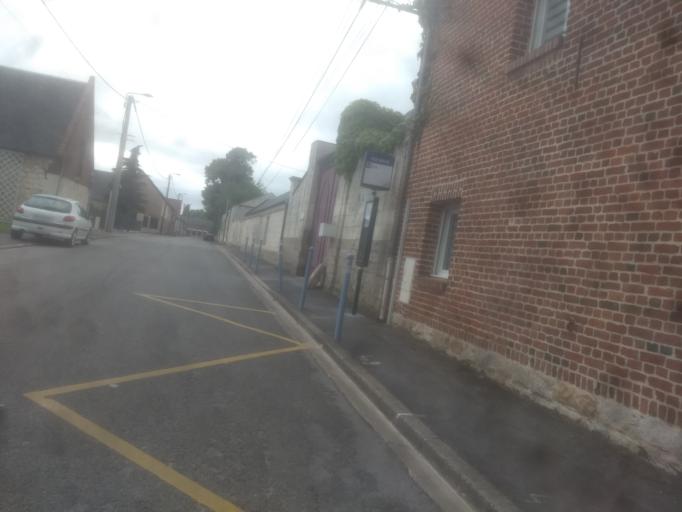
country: FR
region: Nord-Pas-de-Calais
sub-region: Departement du Pas-de-Calais
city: Maroeuil
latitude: 50.3254
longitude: 2.7033
